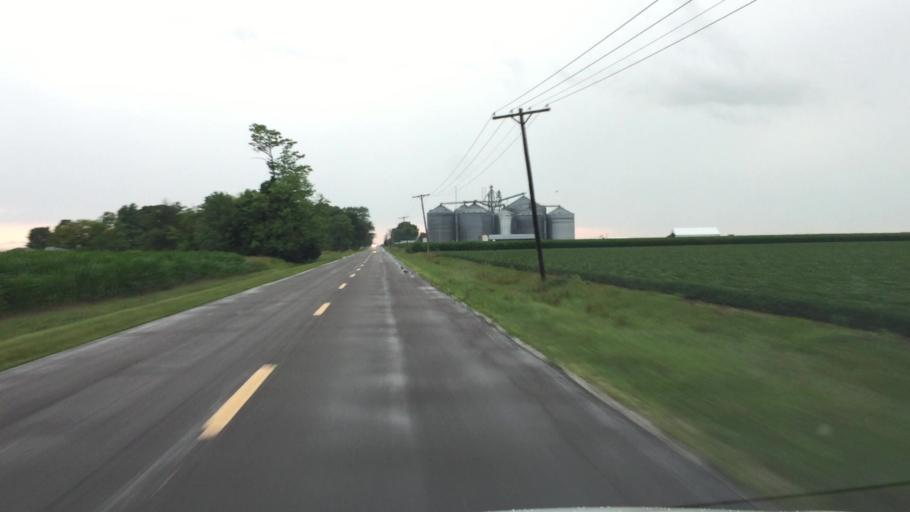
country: US
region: Illinois
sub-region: Hancock County
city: Carthage
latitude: 40.5207
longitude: -91.1605
